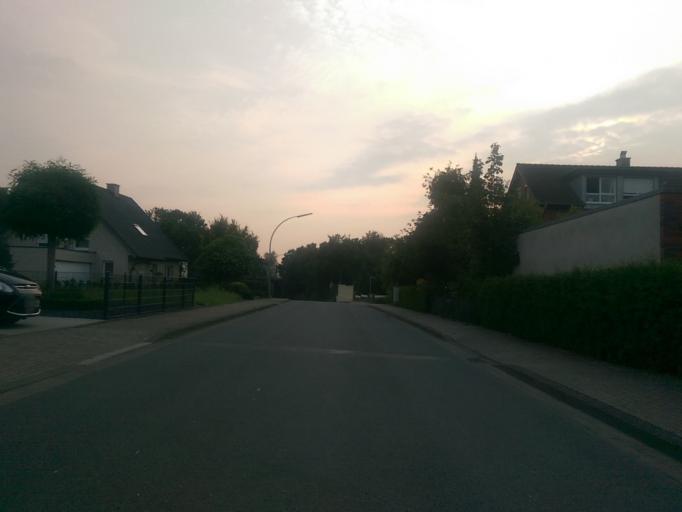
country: DE
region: North Rhine-Westphalia
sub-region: Regierungsbezirk Detmold
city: Rheda-Wiedenbruck
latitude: 51.8616
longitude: 8.3180
